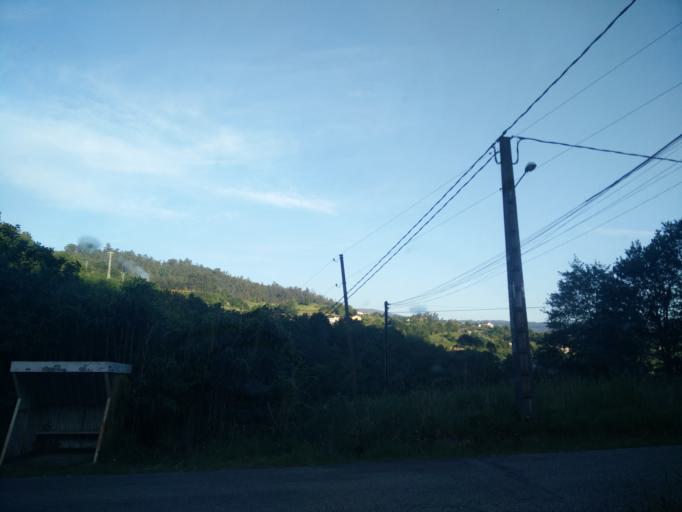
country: ES
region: Galicia
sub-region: Provincia de Pontevedra
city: Mondariz
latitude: 42.2702
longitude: -8.4070
